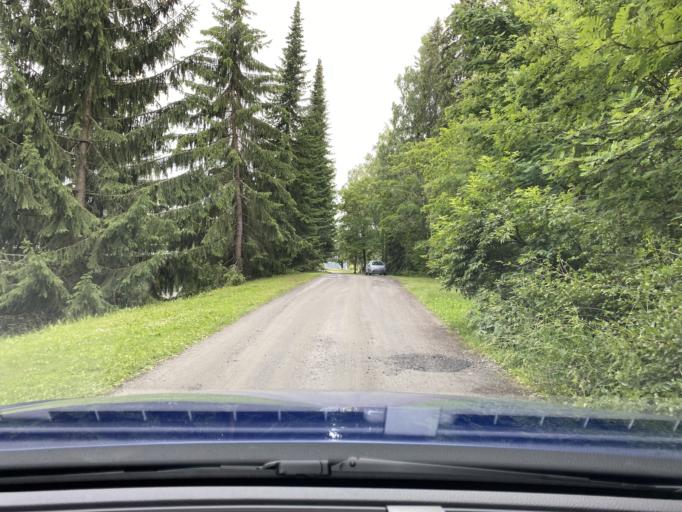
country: FI
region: Pirkanmaa
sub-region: Tampere
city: Lempaeaelae
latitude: 61.3080
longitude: 23.7501
